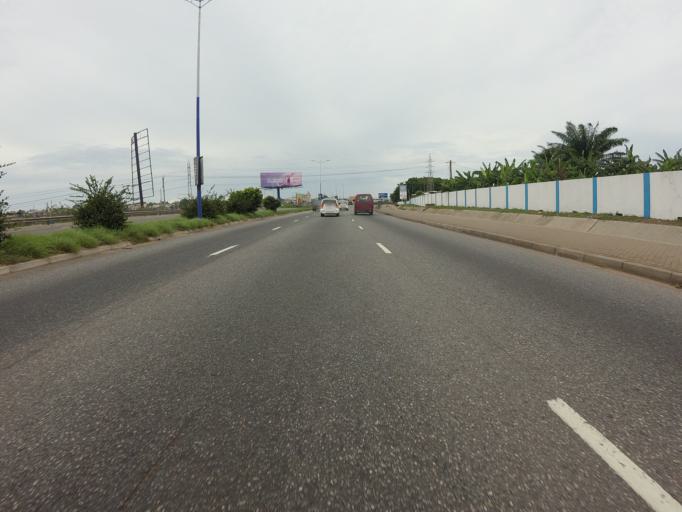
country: GH
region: Greater Accra
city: Accra
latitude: 5.5916
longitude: -0.2195
